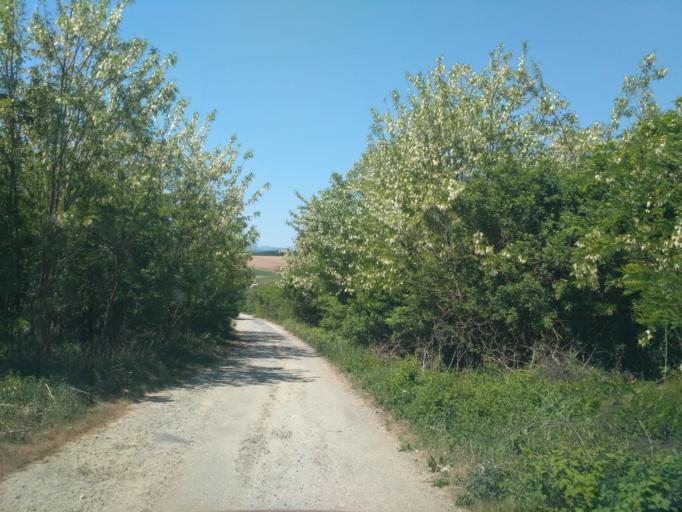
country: SK
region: Kosicky
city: Kosice
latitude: 48.7921
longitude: 21.3653
